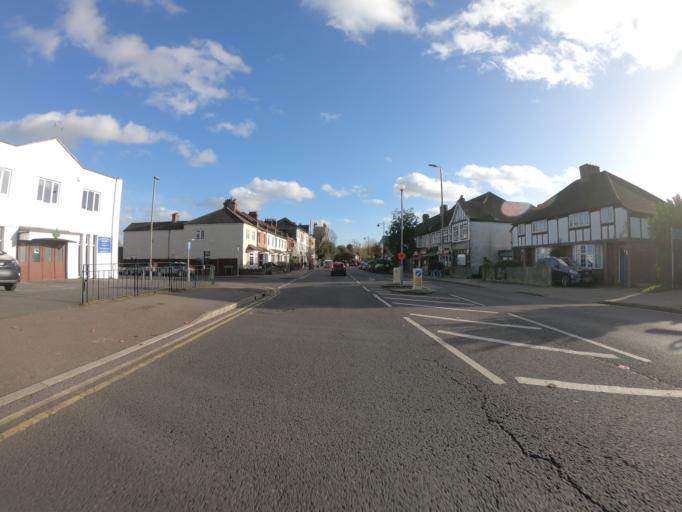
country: GB
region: England
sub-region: Greater London
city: Chislehurst
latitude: 51.4202
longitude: 0.0651
